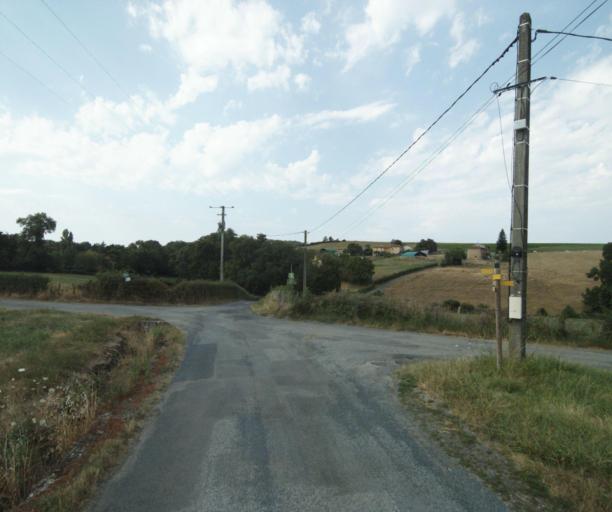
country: FR
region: Rhone-Alpes
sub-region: Departement du Rhone
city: Bully
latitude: 45.8596
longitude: 4.5867
